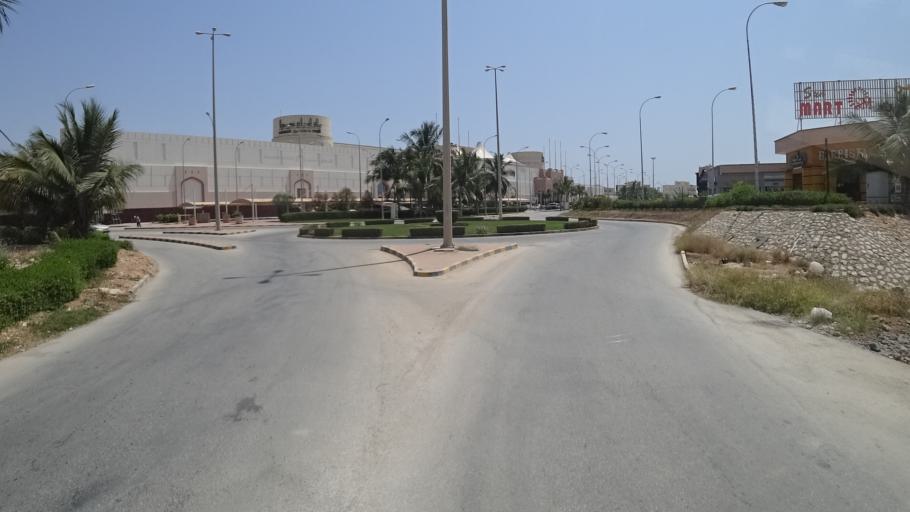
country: OM
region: Zufar
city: Salalah
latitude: 17.0235
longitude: 54.0636
